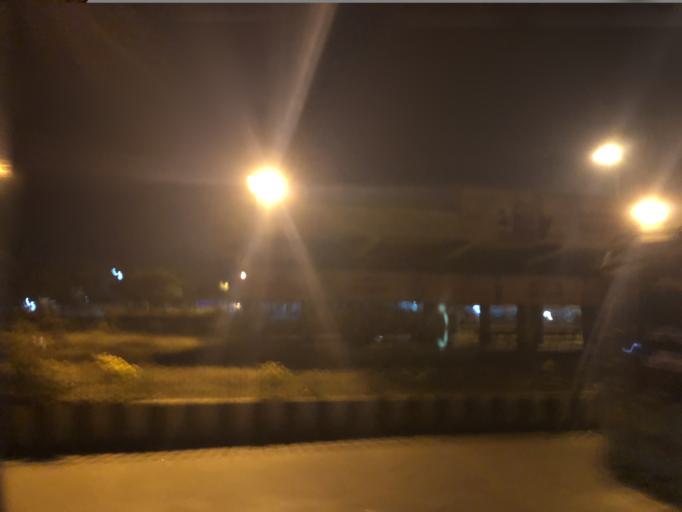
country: IN
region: Tamil Nadu
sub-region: Thanjavur
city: Thanjavur
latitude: 10.7501
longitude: 79.1112
